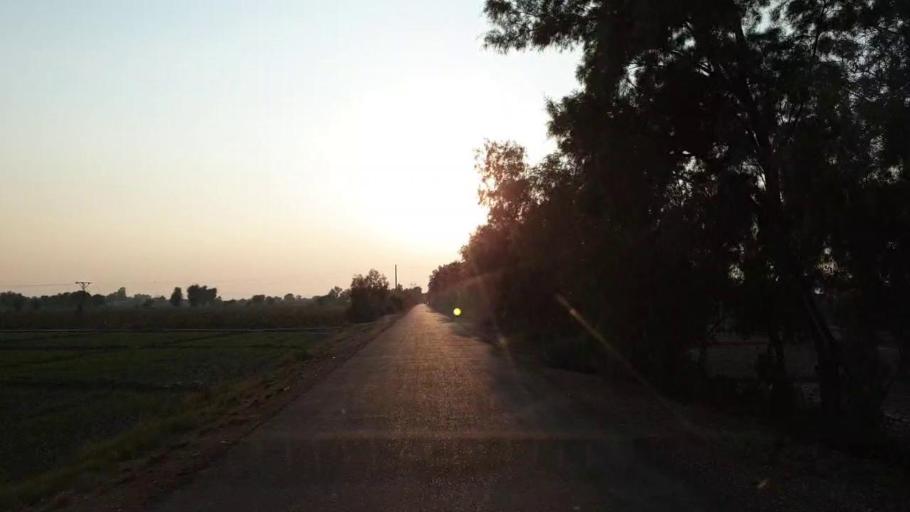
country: PK
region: Sindh
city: Sehwan
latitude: 26.4539
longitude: 67.7722
